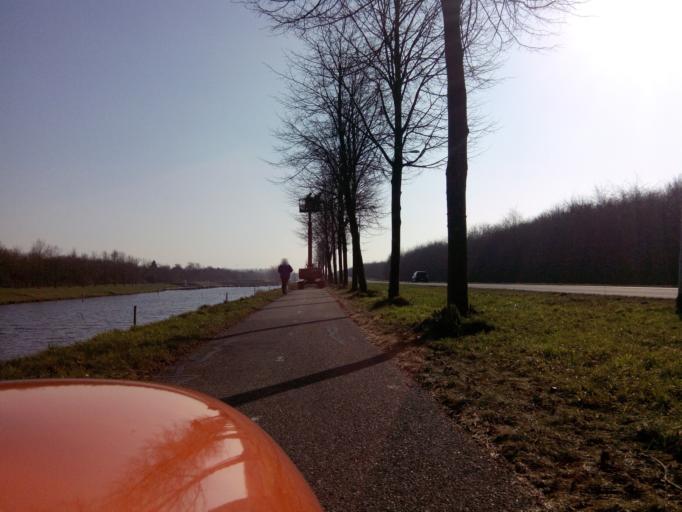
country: NL
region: Flevoland
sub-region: Gemeente Zeewolde
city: Zeewolde
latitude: 52.3387
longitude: 5.5104
